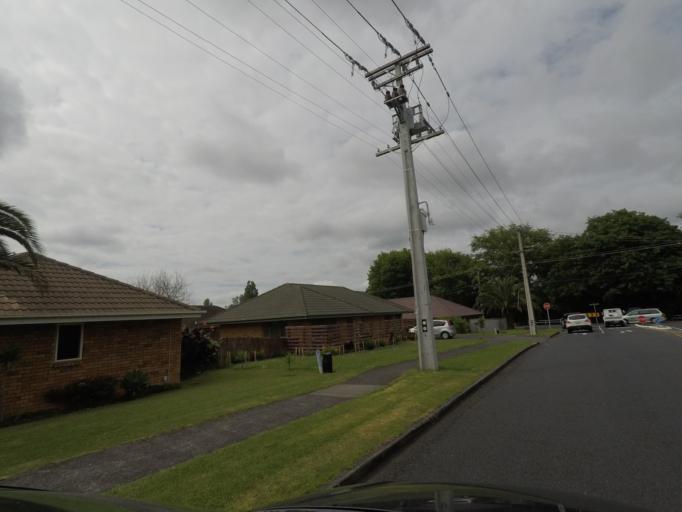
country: NZ
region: Auckland
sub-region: Auckland
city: Waitakere
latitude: -36.9030
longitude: 174.6213
